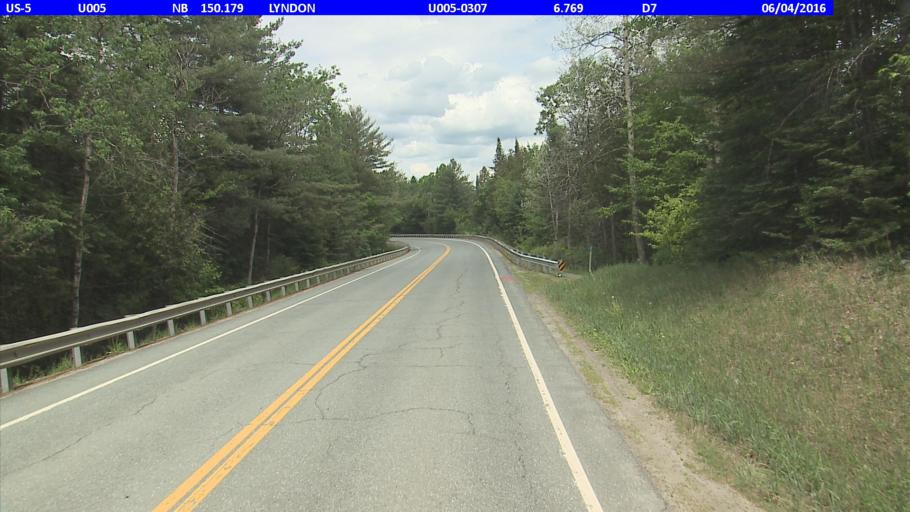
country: US
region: Vermont
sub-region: Caledonia County
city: Lyndonville
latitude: 44.5843
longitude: -71.9826
